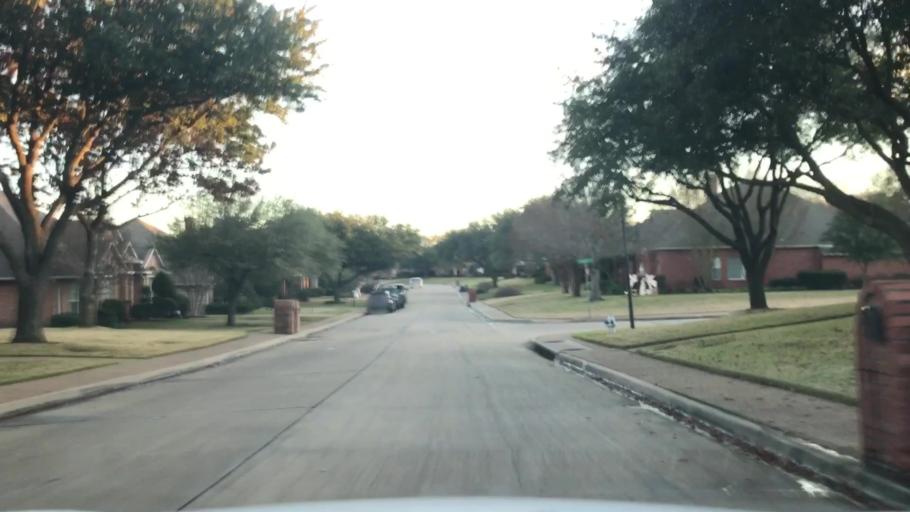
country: US
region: Texas
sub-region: Rockwall County
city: Rockwall
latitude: 32.8846
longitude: -96.4714
